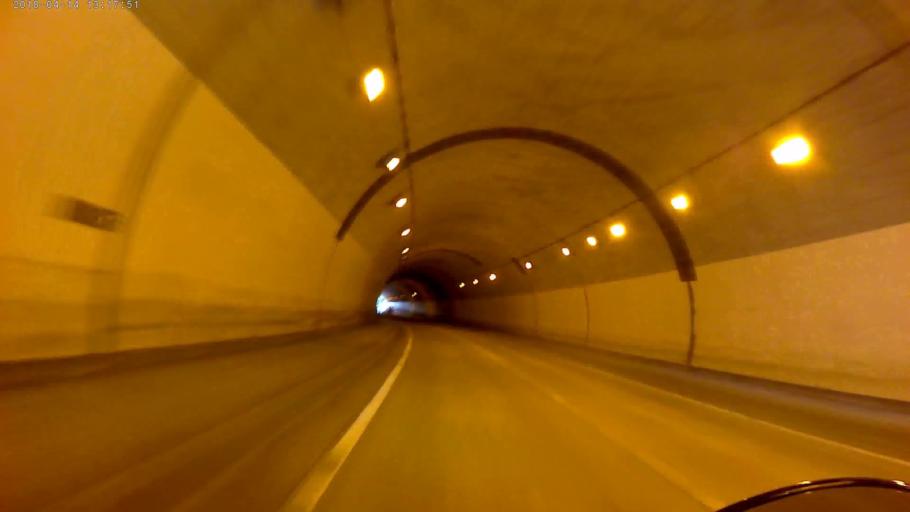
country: JP
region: Kanagawa
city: Hadano
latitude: 35.3400
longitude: 139.2269
